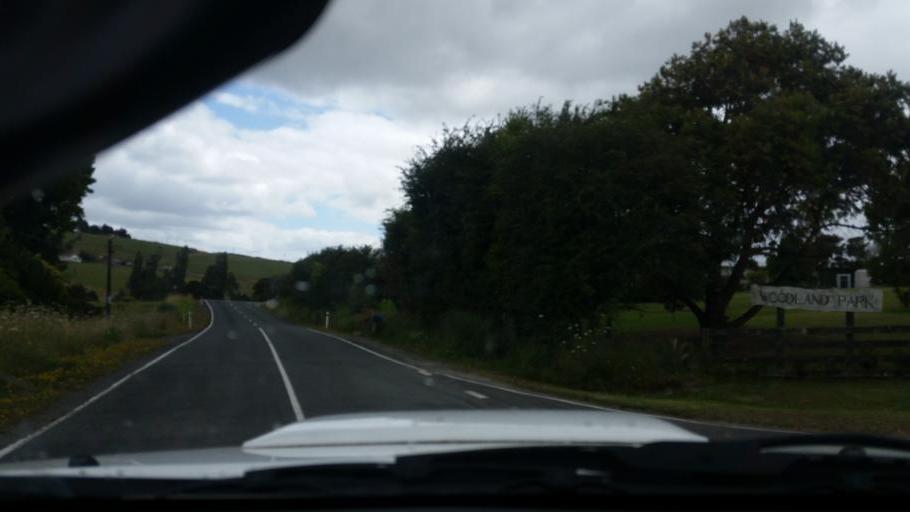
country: NZ
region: Northland
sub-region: Whangarei
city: Ruakaka
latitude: -36.0973
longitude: 174.3509
